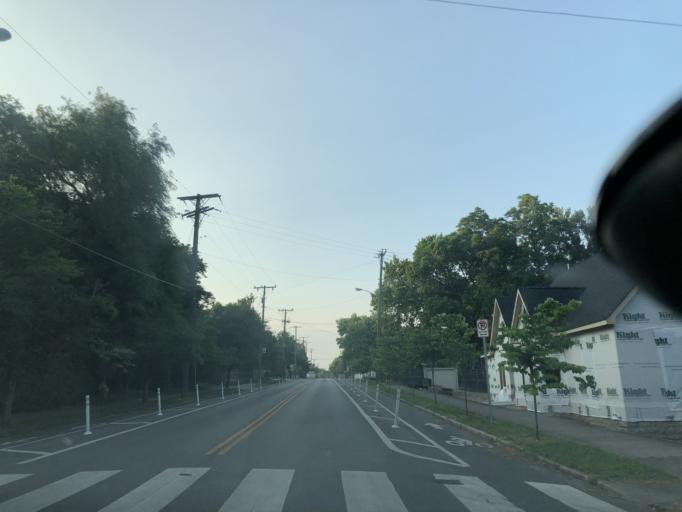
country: US
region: Tennessee
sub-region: Davidson County
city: Oak Hill
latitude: 36.1234
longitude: -86.7864
